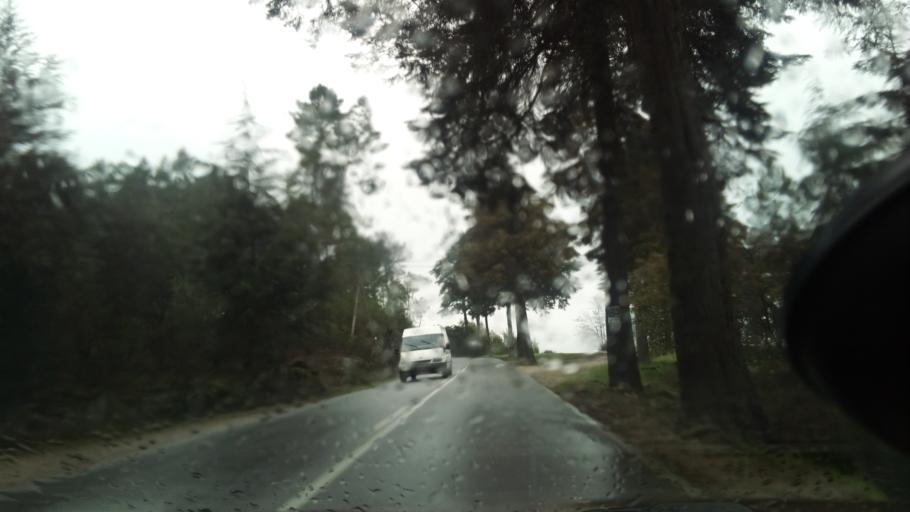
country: PT
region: Viseu
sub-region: Mangualde
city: Mangualde
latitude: 40.6092
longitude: -7.6891
